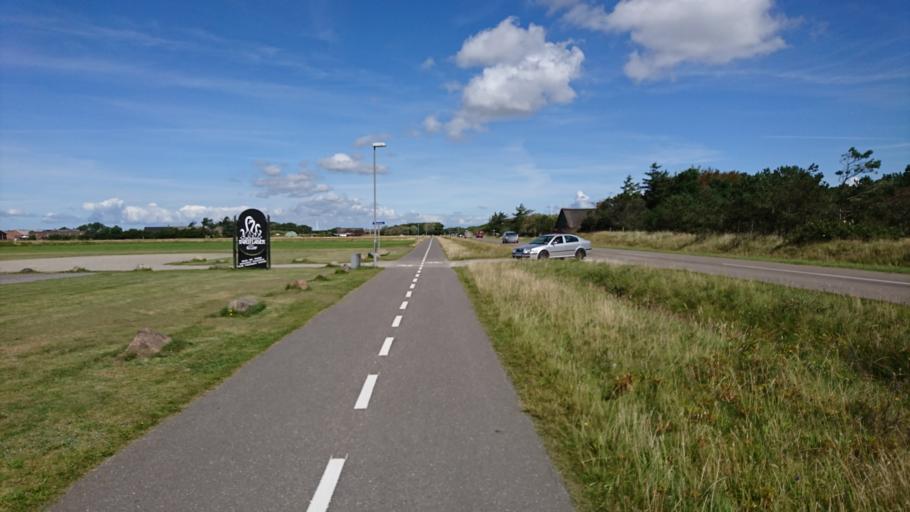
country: DK
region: South Denmark
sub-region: Fano Kommune
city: Nordby
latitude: 55.4208
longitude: 8.3984
